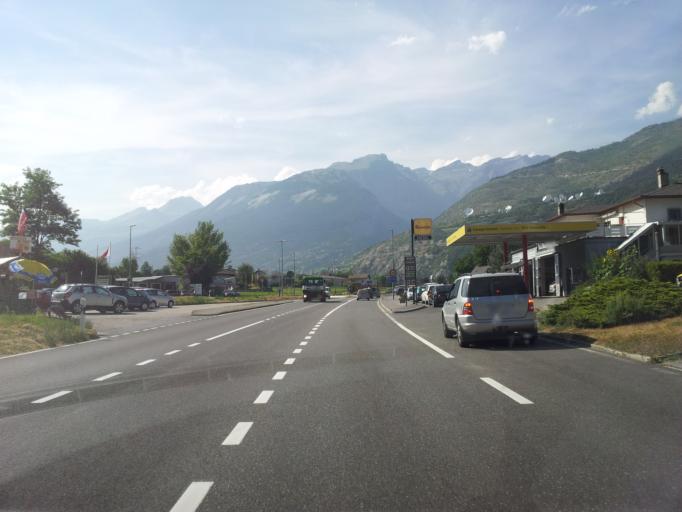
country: CH
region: Valais
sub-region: Leuk District
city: Leuk
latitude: 46.2999
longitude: 7.6597
